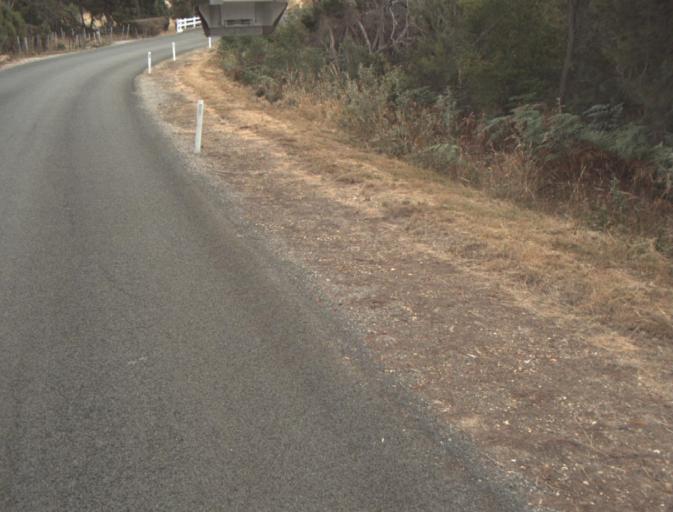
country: AU
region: Tasmania
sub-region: Launceston
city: Mayfield
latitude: -41.2839
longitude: 147.0144
